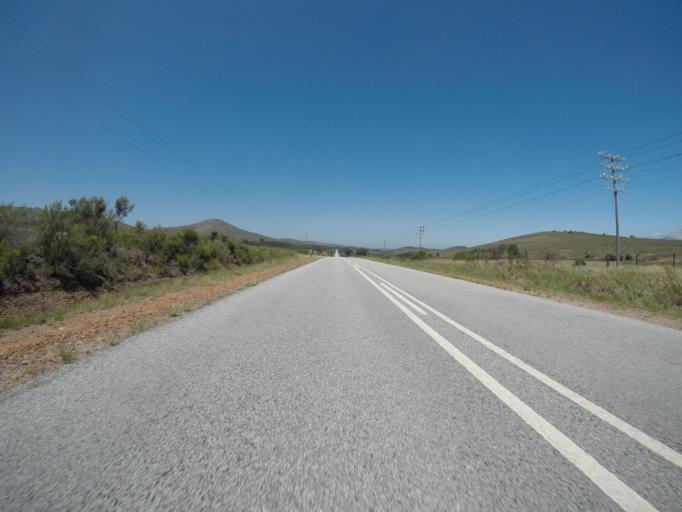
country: ZA
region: Eastern Cape
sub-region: Cacadu District Municipality
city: Kareedouw
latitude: -33.9578
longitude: 24.4023
